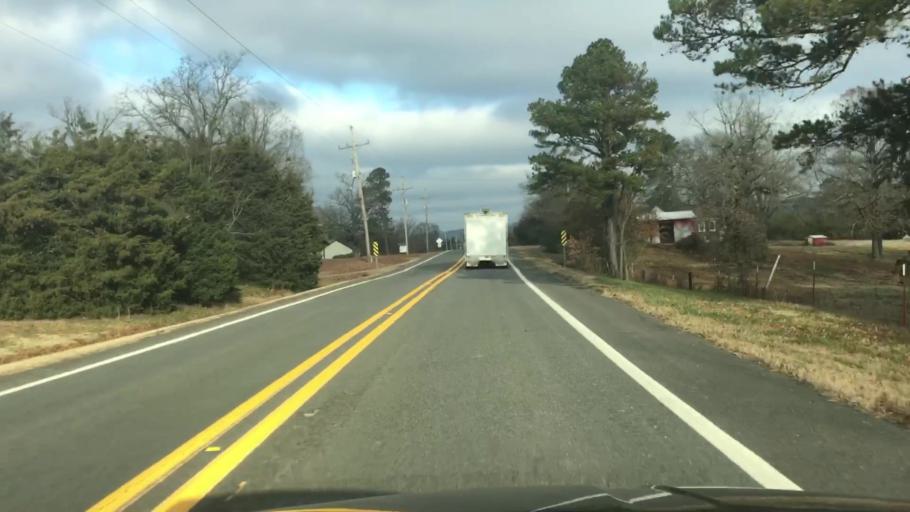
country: US
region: Arkansas
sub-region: Montgomery County
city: Mount Ida
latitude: 34.6258
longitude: -93.7307
